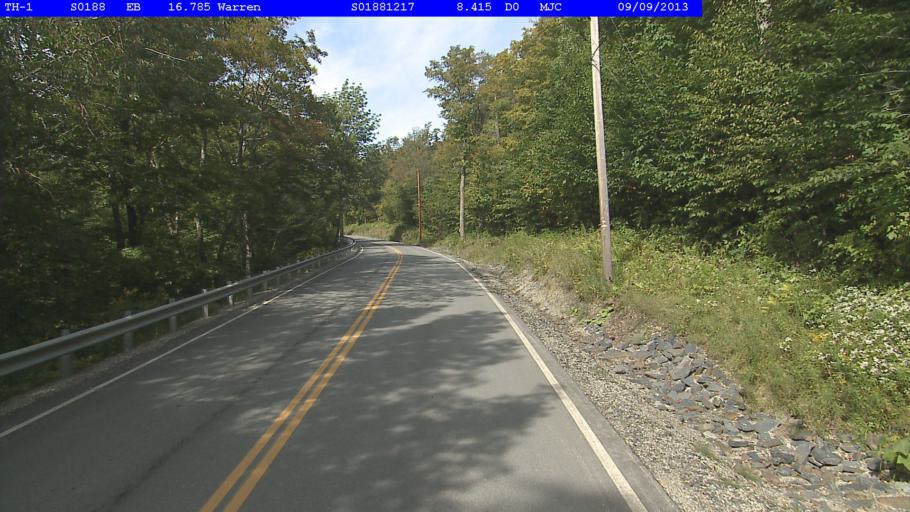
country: US
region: Vermont
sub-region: Washington County
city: Northfield
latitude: 44.1045
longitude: -72.7916
